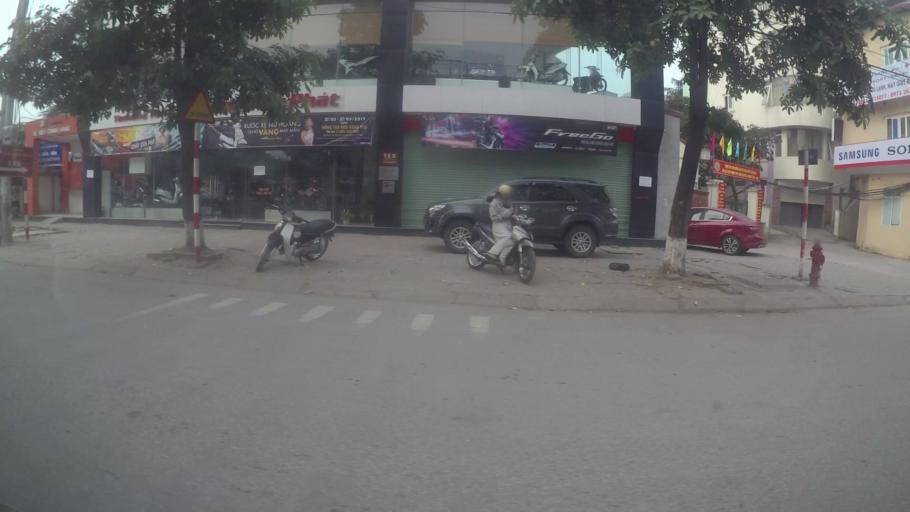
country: VN
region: Ha Noi
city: Cau Dien
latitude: 21.0465
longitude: 105.7489
